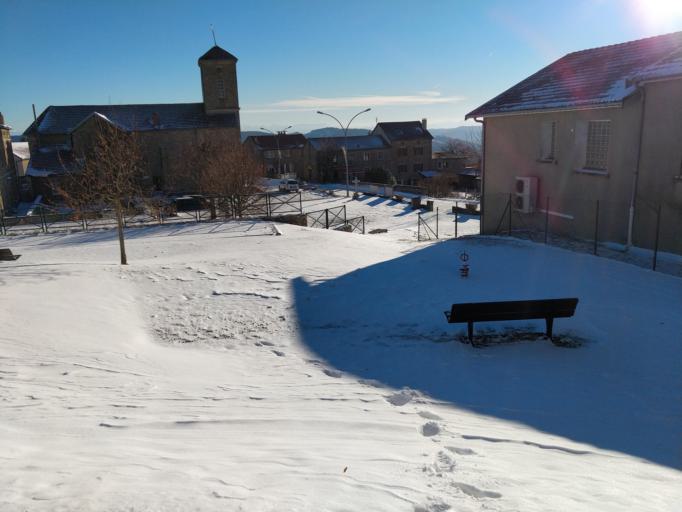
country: FR
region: Rhone-Alpes
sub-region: Departement de l'Ardeche
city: Saint-Agreve
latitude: 45.0467
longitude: 4.4580
